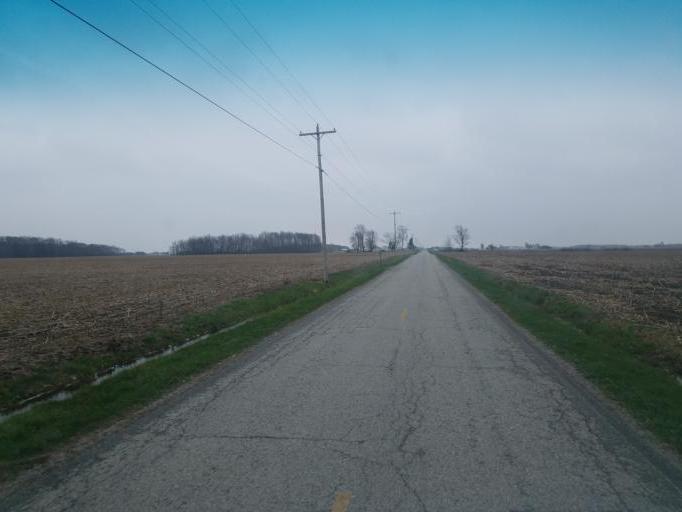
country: US
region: Ohio
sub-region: Marion County
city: Prospect
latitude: 40.4025
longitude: -83.1169
